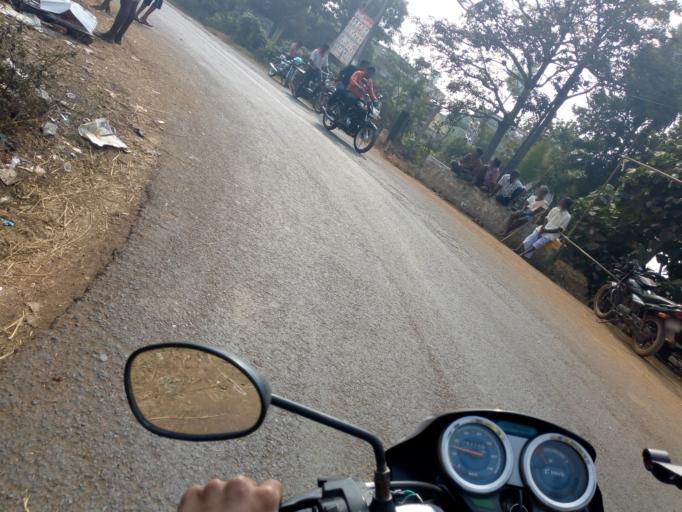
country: IN
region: Andhra Pradesh
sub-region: West Godavari
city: Tadepallegudem
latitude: 16.7765
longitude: 81.4218
